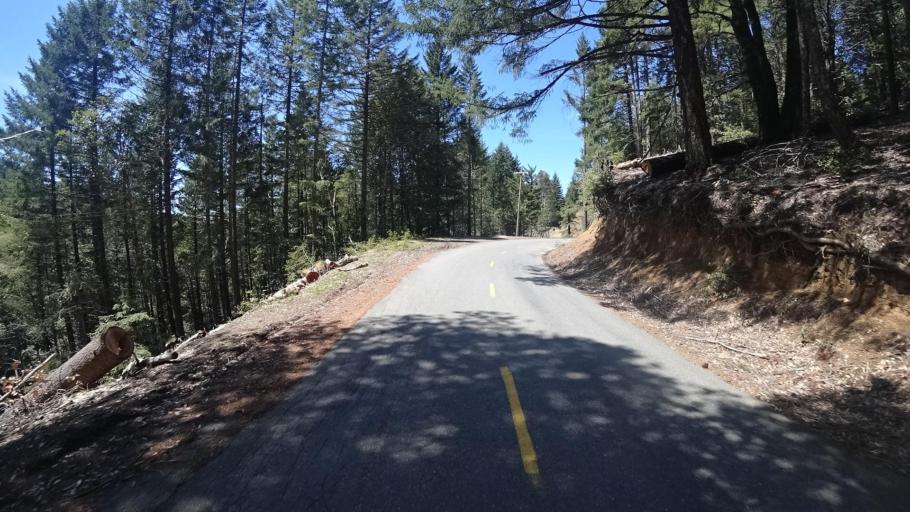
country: US
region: California
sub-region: Humboldt County
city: Rio Dell
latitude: 40.2863
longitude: -124.0549
